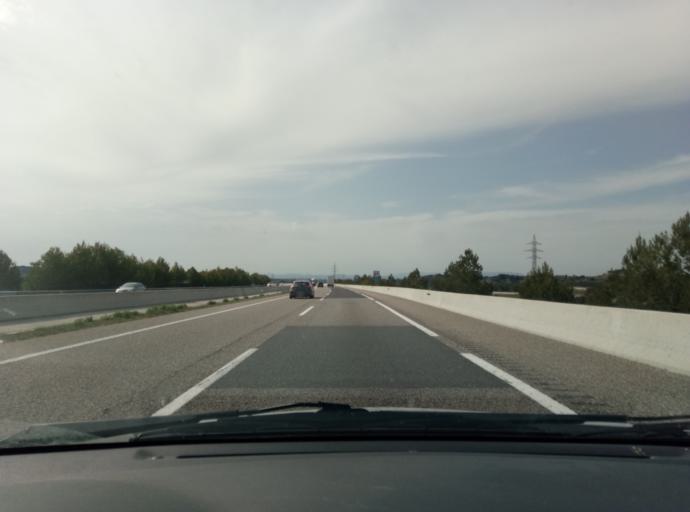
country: ES
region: Catalonia
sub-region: Provincia de Lleida
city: Sant Guim de Freixenet
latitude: 41.6270
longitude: 1.3742
